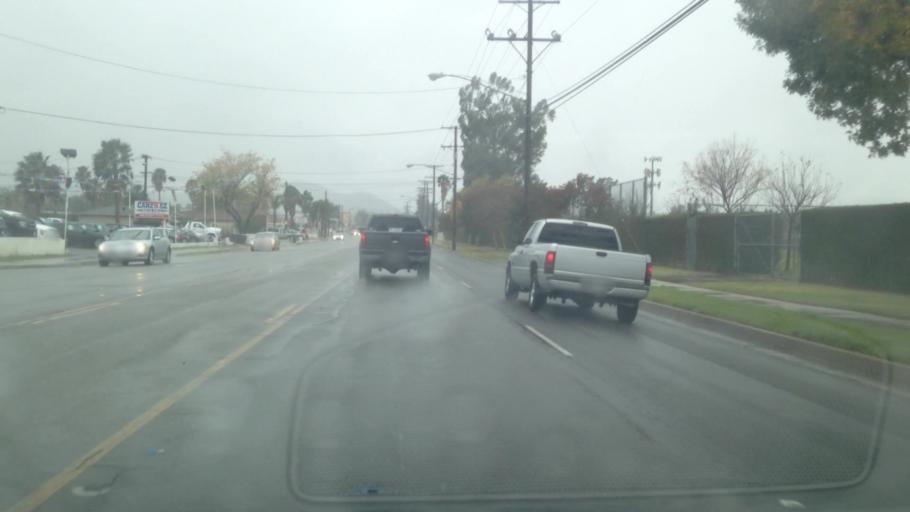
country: US
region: California
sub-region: Riverside County
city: Pedley
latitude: 33.9466
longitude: -117.4736
